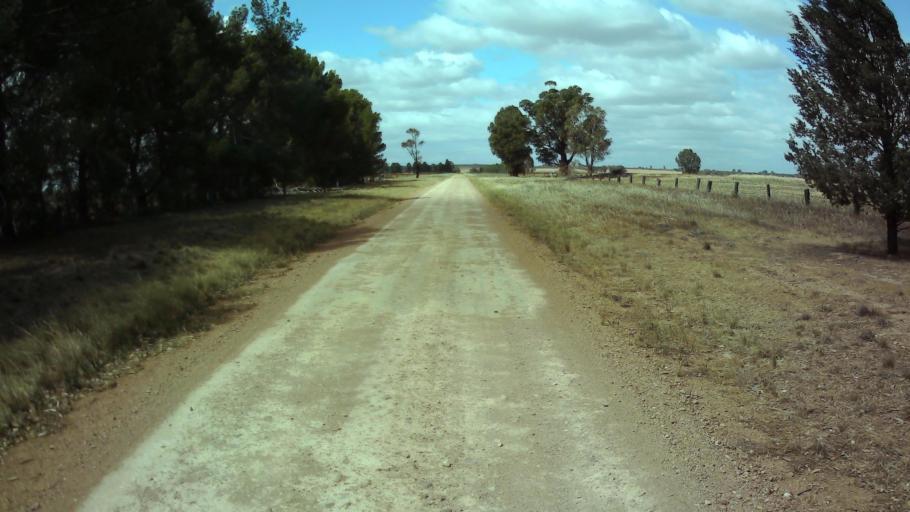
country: AU
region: New South Wales
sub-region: Weddin
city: Grenfell
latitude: -34.0505
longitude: 148.3321
